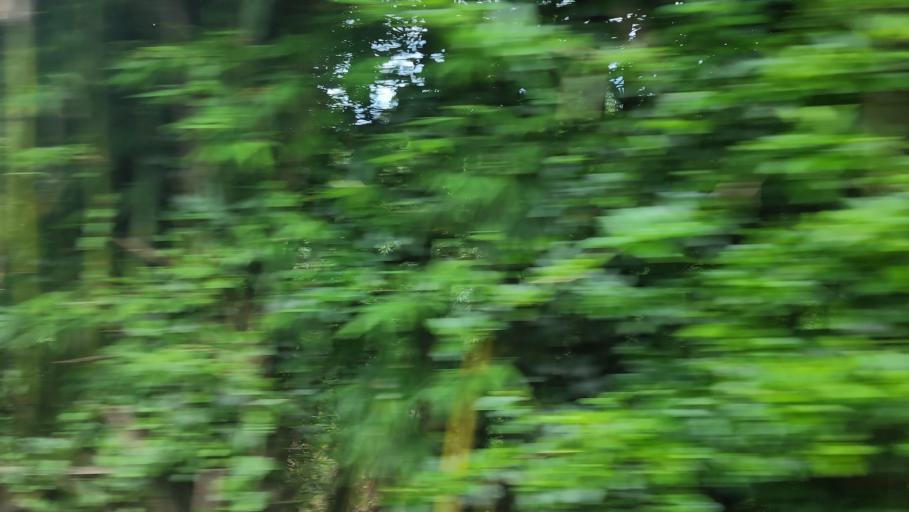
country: TW
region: Taiwan
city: Daxi
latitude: 24.8833
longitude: 121.4184
